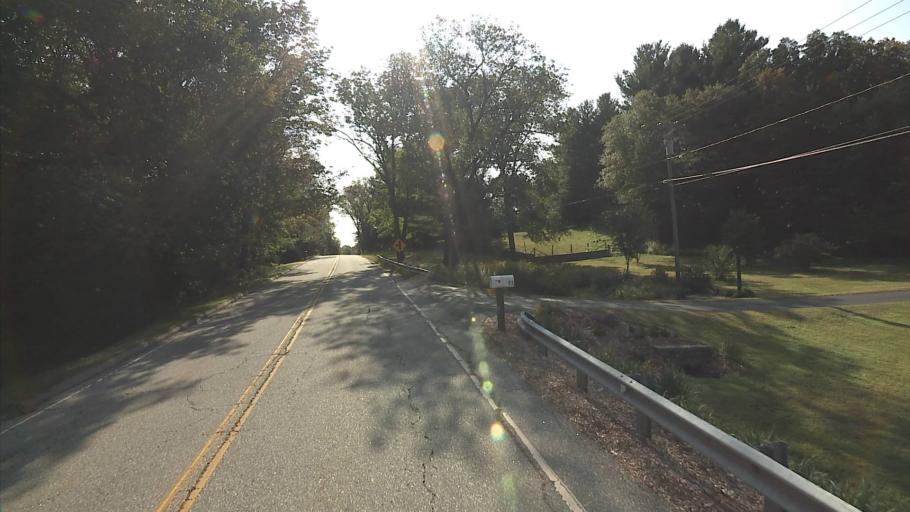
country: US
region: Connecticut
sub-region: Windham County
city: Willimantic
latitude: 41.6700
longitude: -72.2622
